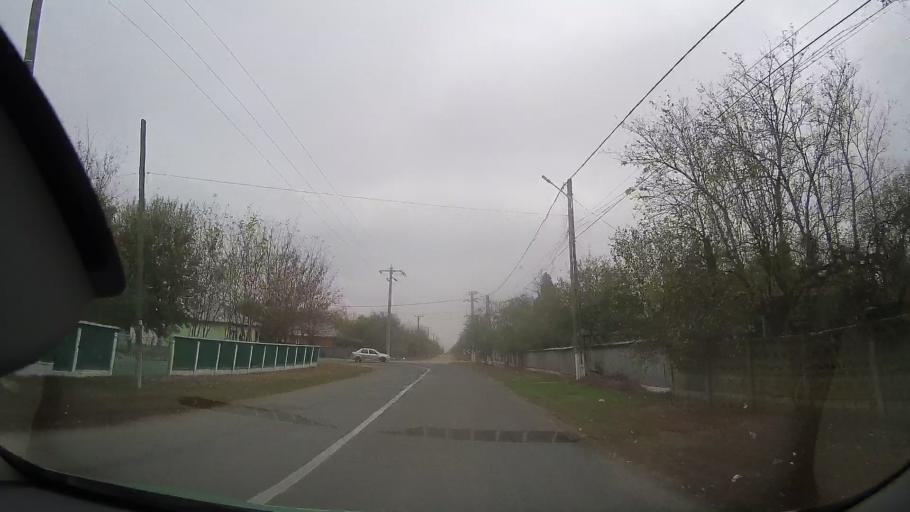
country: RO
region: Ialomita
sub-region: Comuna Grindu
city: Grindu
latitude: 44.7760
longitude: 26.9049
